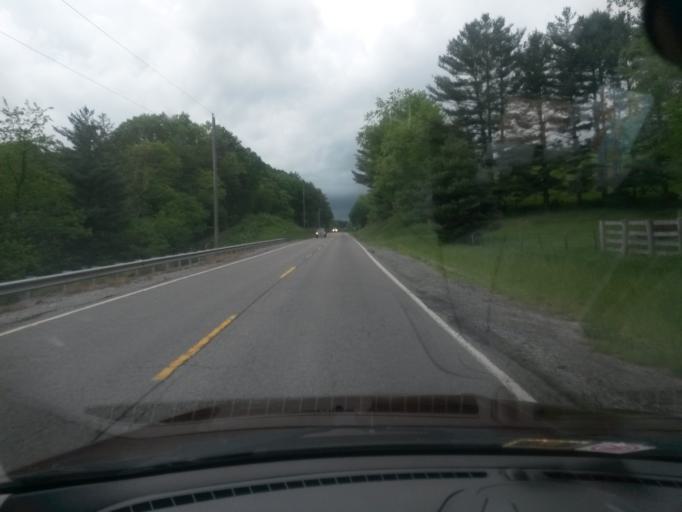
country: US
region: Virginia
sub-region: Floyd County
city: Floyd
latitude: 36.9413
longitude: -80.3505
